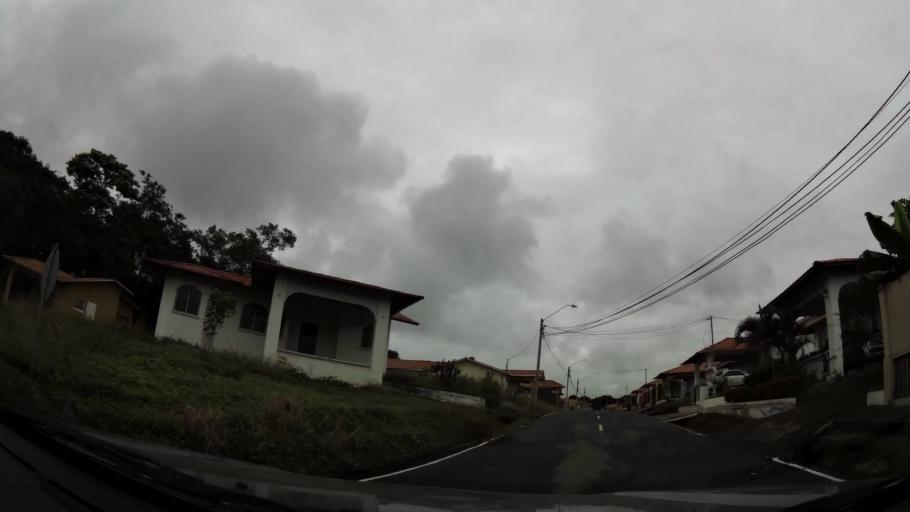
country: PA
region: Chiriqui
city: David
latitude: 8.4377
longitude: -82.4438
